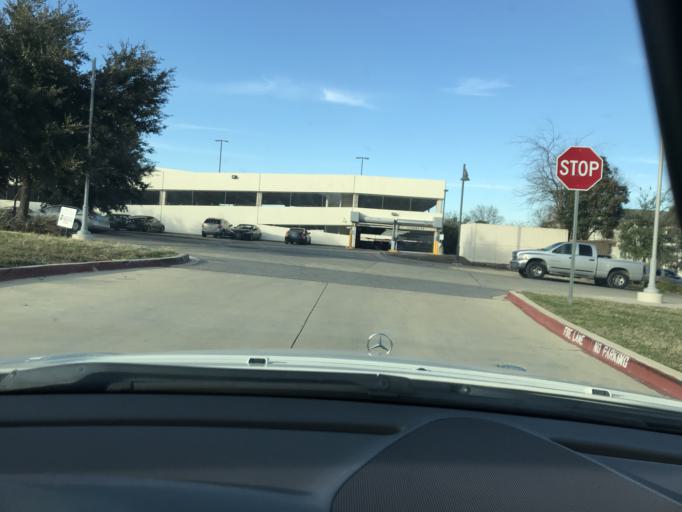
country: US
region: Texas
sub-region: Dallas County
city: University Park
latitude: 32.8914
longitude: -96.7674
